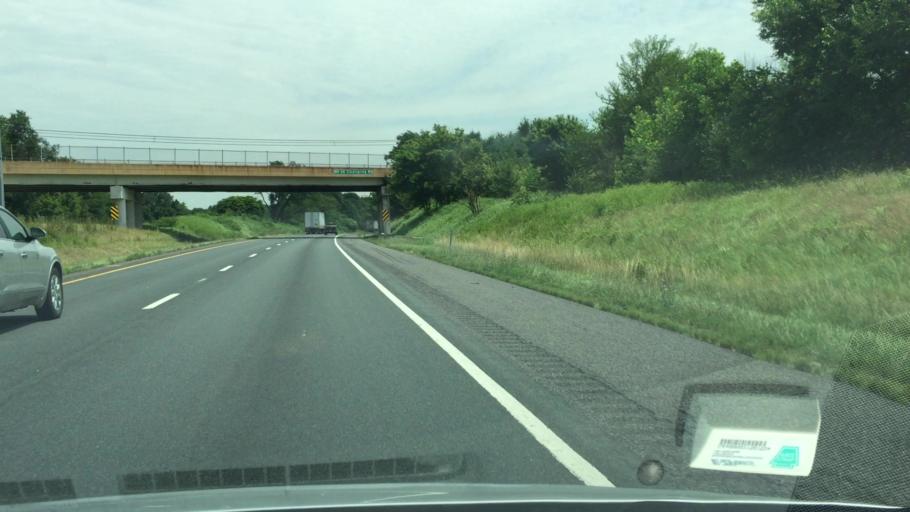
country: US
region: Maryland
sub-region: Washington County
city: Wilson-Conococheague
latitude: 39.6511
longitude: -77.9242
